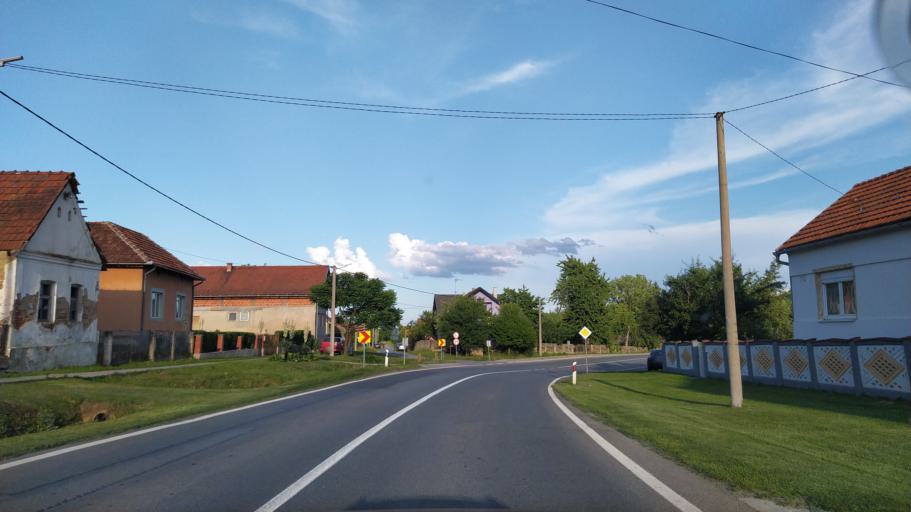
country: HR
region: Virovitick-Podravska
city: Cacinci
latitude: 45.6128
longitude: 17.8095
